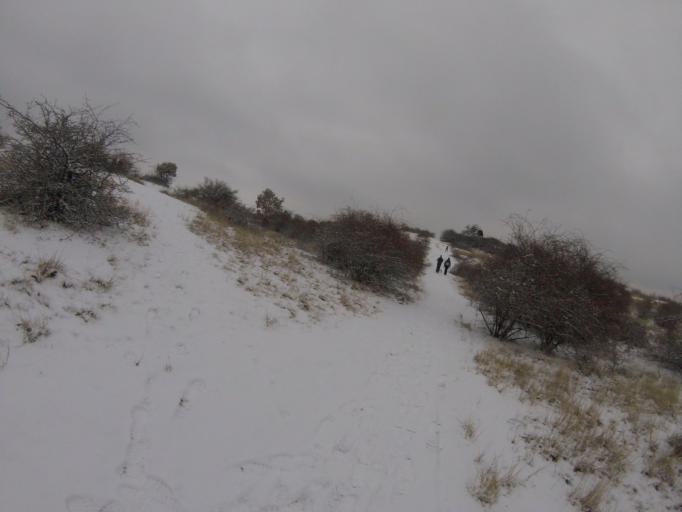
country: HU
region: Fejer
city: Pakozd
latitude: 47.2349
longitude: 18.5377
